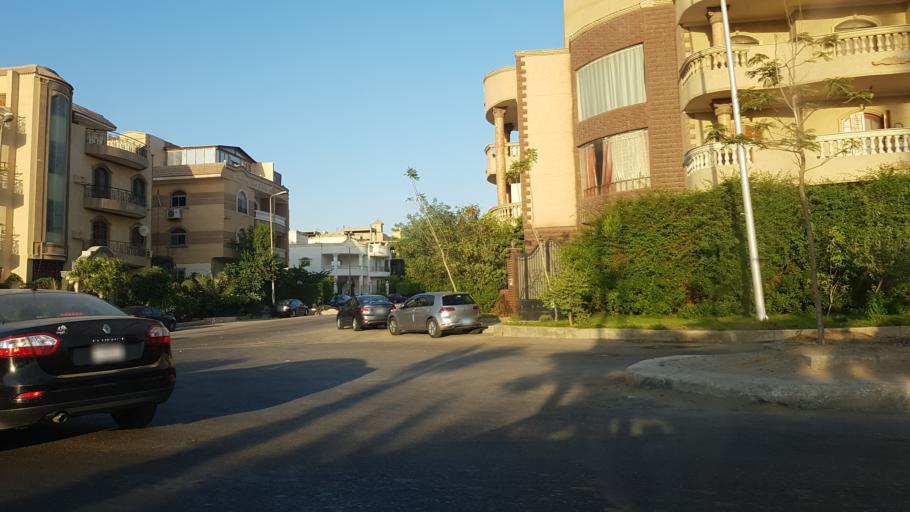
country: EG
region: Muhafazat al Qalyubiyah
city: Al Khankah
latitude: 30.0552
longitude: 31.4427
